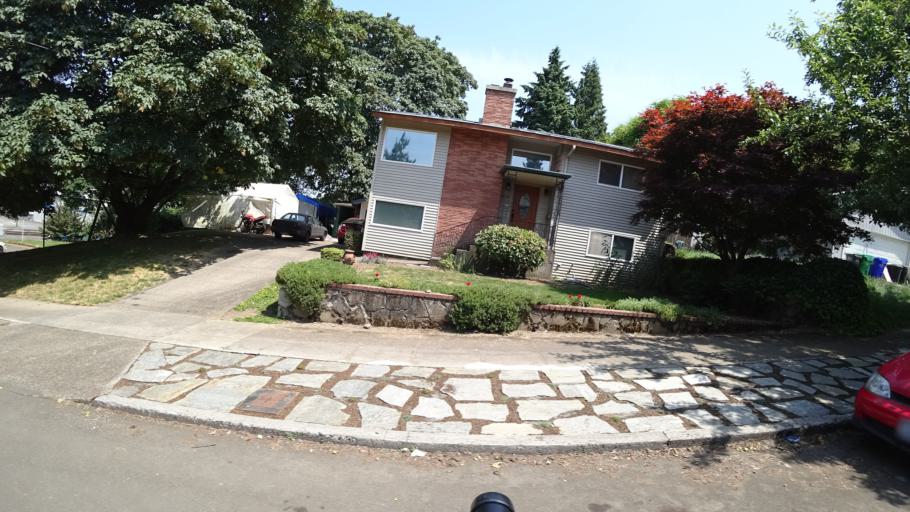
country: US
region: Washington
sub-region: Clark County
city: Vancouver
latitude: 45.5869
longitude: -122.6941
